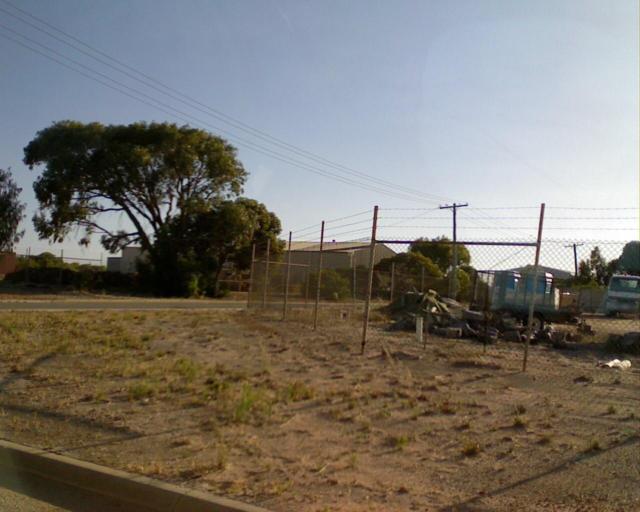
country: AU
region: Western Australia
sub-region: Dandaragan
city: Jurien Bay
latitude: -30.0523
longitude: 114.9778
